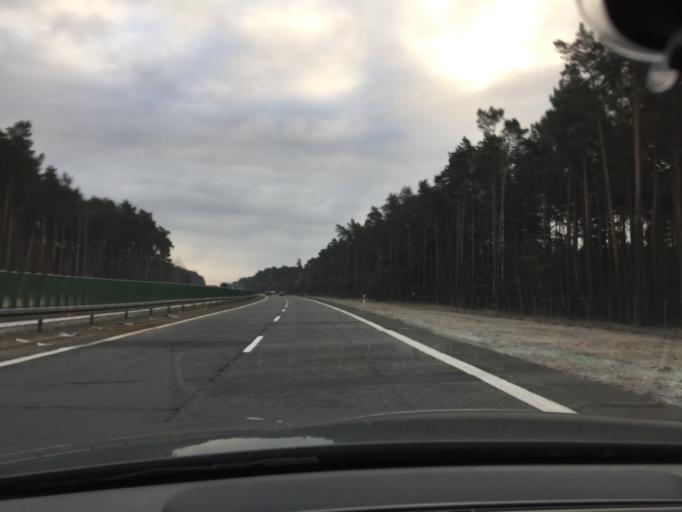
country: PL
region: Lubusz
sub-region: Powiat zarski
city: Lipinki Luzyckie
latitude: 51.6143
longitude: 14.9272
